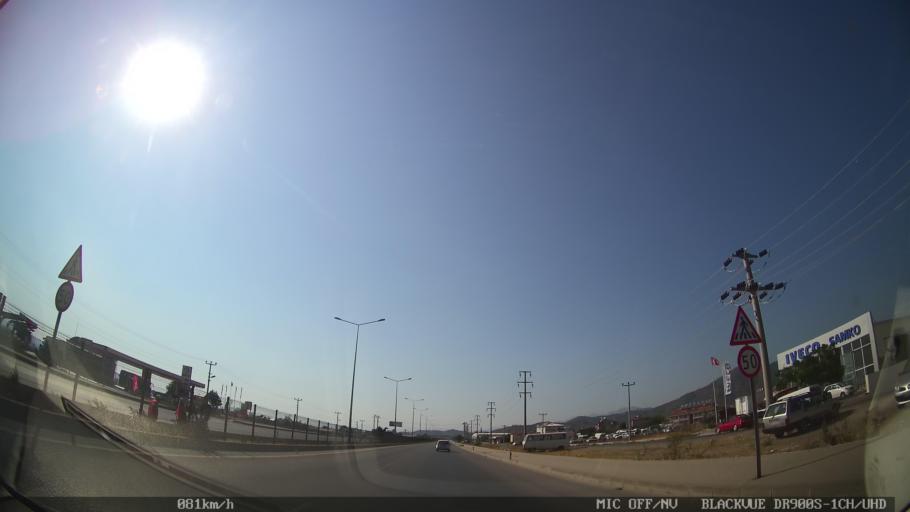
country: TR
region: Mugla
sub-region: Fethiye
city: Fethiye
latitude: 36.6568
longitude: 29.1599
